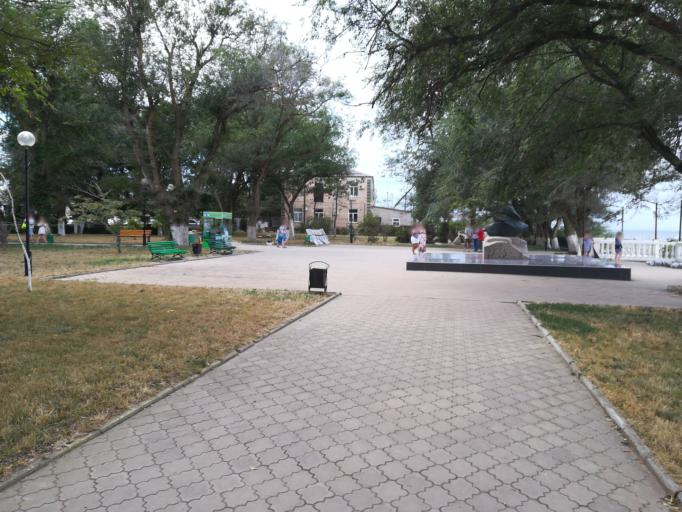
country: RU
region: Krasnodarskiy
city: Taman'
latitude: 45.2181
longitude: 36.7251
